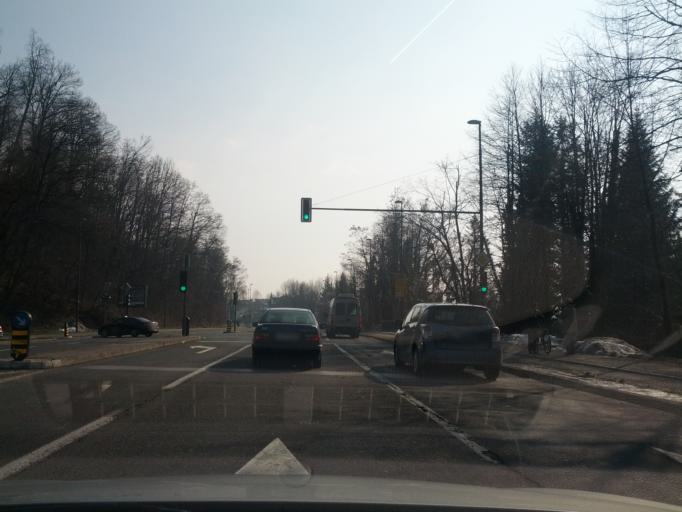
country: SI
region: Ljubljana
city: Ljubljana
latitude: 46.0416
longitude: 14.5150
